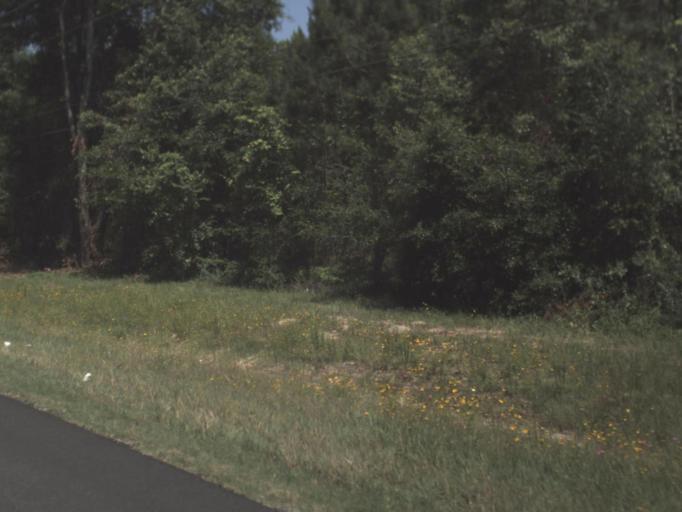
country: US
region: Florida
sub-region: Suwannee County
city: Wellborn
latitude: 30.1947
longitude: -82.7552
